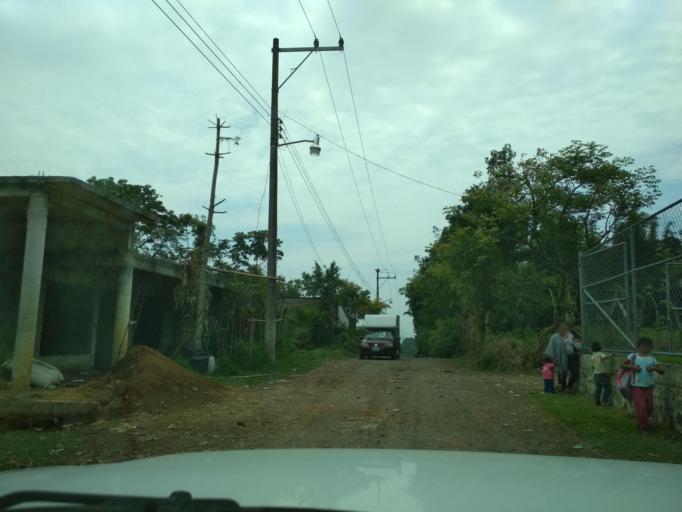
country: MX
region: Veracruz
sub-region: La Perla
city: La Perla
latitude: 18.9239
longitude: -97.1268
